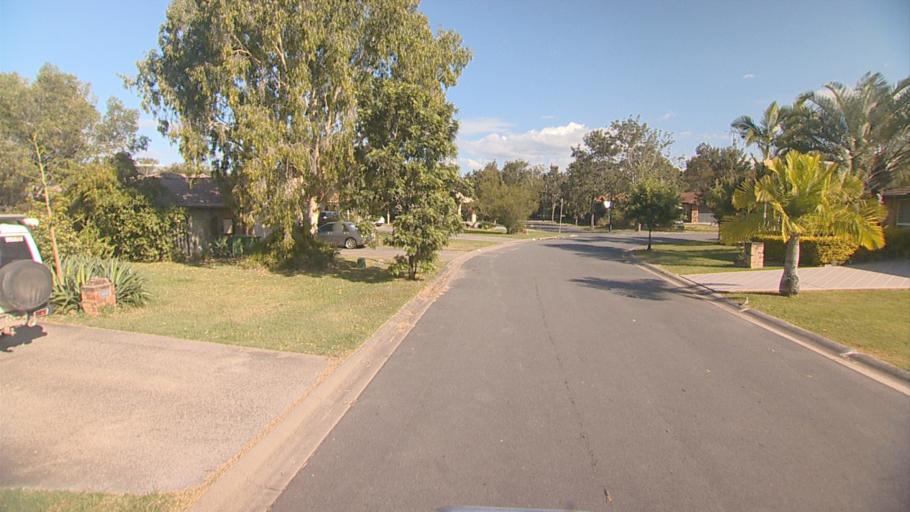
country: AU
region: Queensland
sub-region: Logan
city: Windaroo
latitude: -27.7522
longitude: 153.1953
